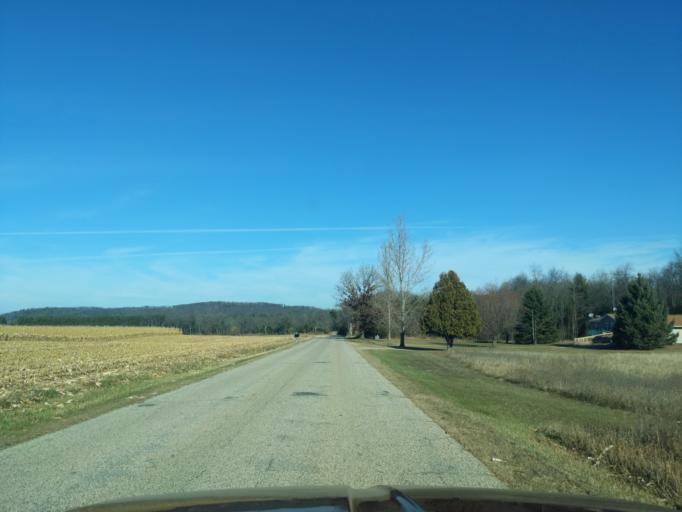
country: US
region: Wisconsin
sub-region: Waushara County
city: Silver Lake
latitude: 44.1000
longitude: -89.1788
